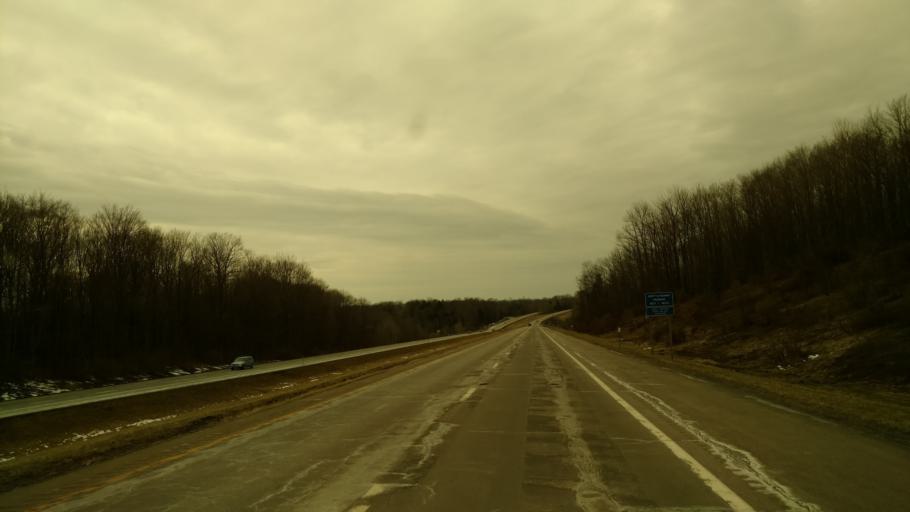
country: US
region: New York
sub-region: Chautauqua County
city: Lakewood
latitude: 42.1363
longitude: -79.3375
